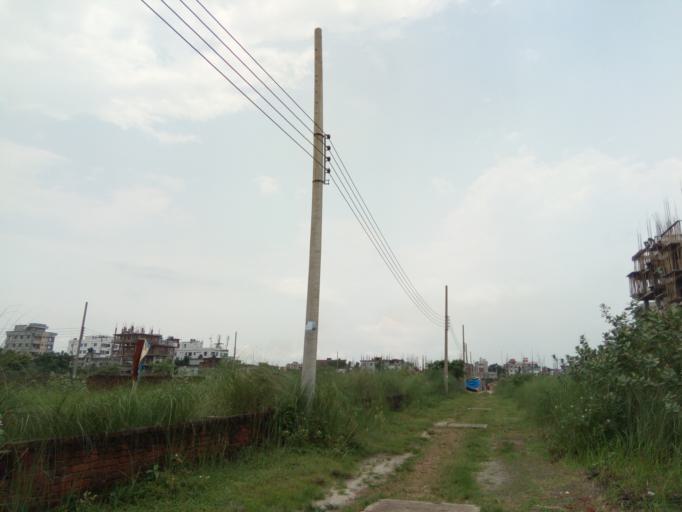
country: BD
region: Dhaka
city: Azimpur
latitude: 23.7482
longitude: 90.3482
